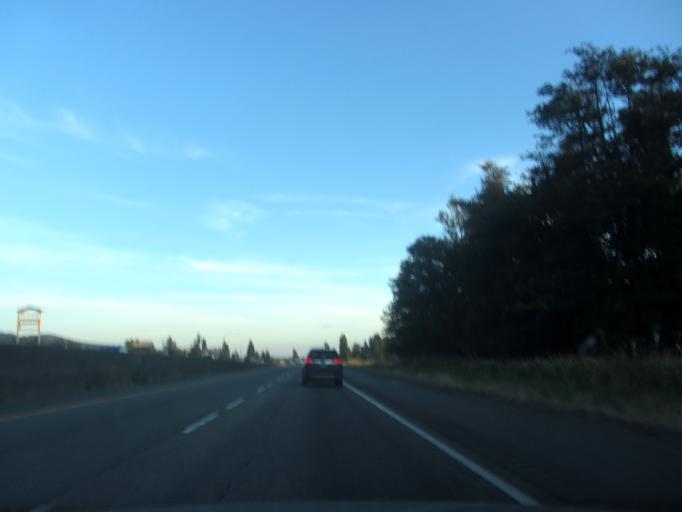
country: US
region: Washington
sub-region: Skagit County
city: Mount Vernon
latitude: 48.4060
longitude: -122.3311
